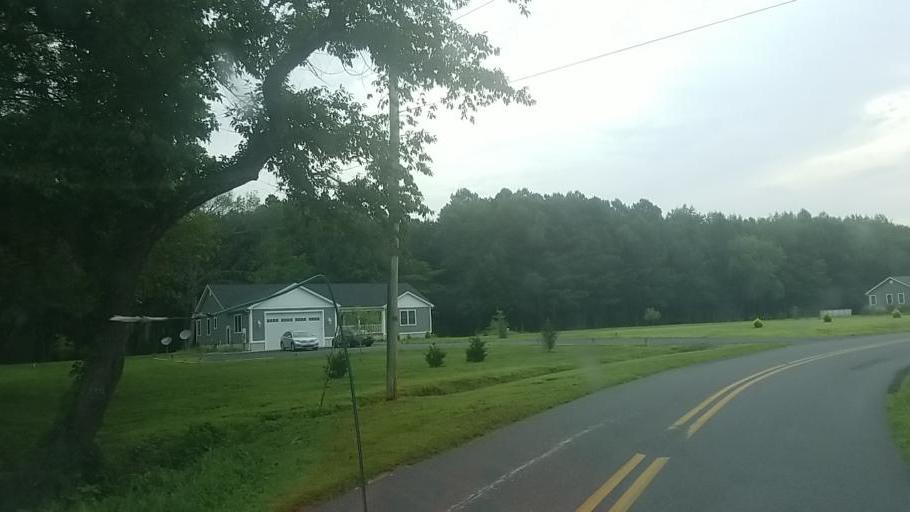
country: US
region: Delaware
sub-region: Sussex County
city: Selbyville
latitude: 38.4438
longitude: -75.2024
